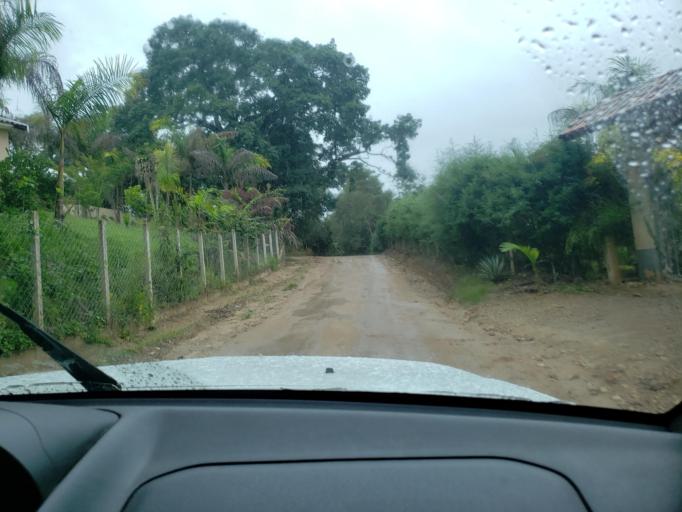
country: BR
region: Minas Gerais
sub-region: Monte Siao
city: Monte Siao
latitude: -22.3816
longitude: -46.5540
